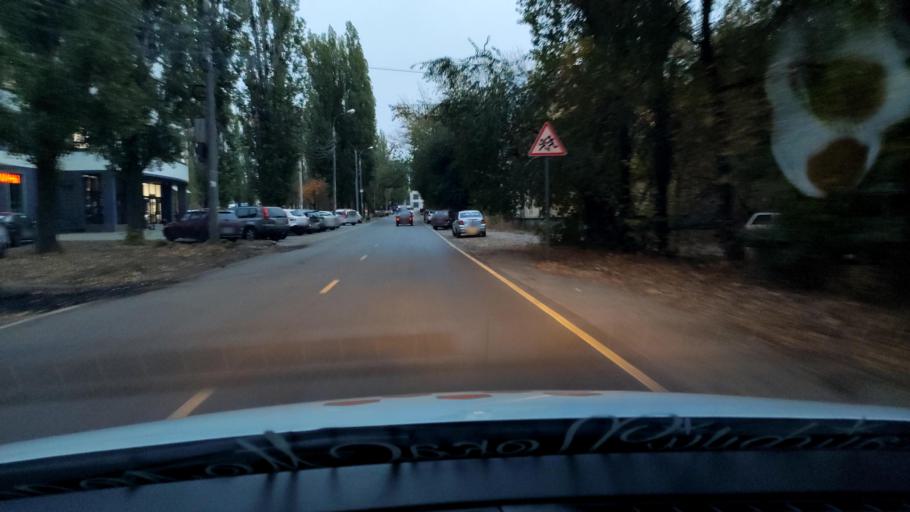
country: RU
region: Voronezj
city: Voronezh
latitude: 51.6776
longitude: 39.1661
